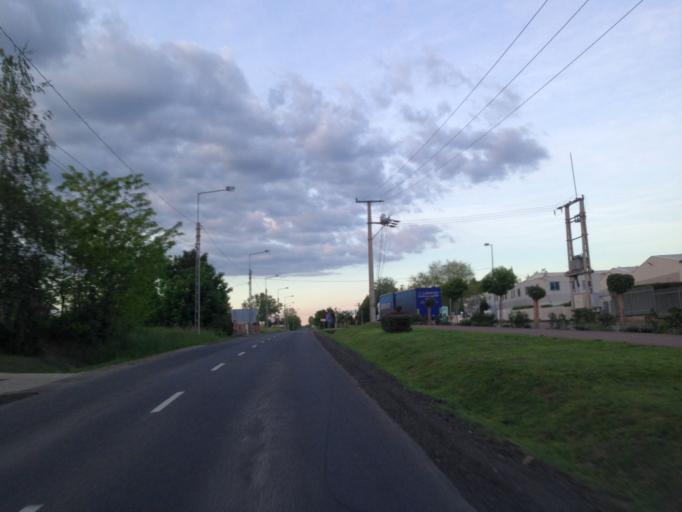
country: HU
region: Nograd
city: Paszto
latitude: 47.9304
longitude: 19.7107
